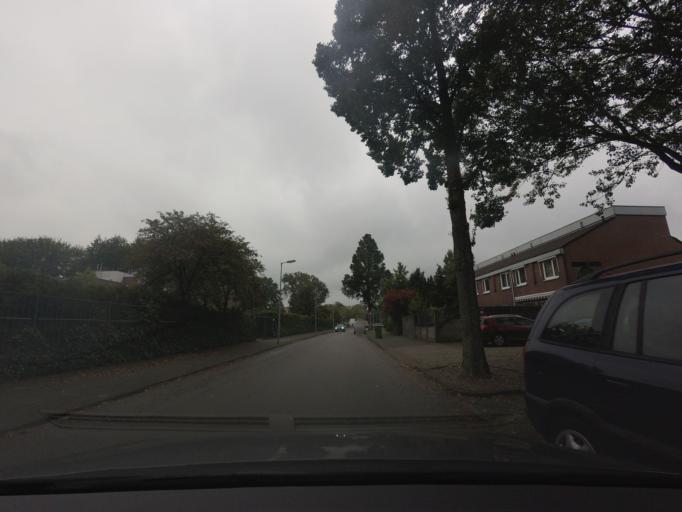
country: NL
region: North Holland
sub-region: Gemeente Alkmaar
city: Alkmaar
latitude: 52.6252
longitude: 4.7200
